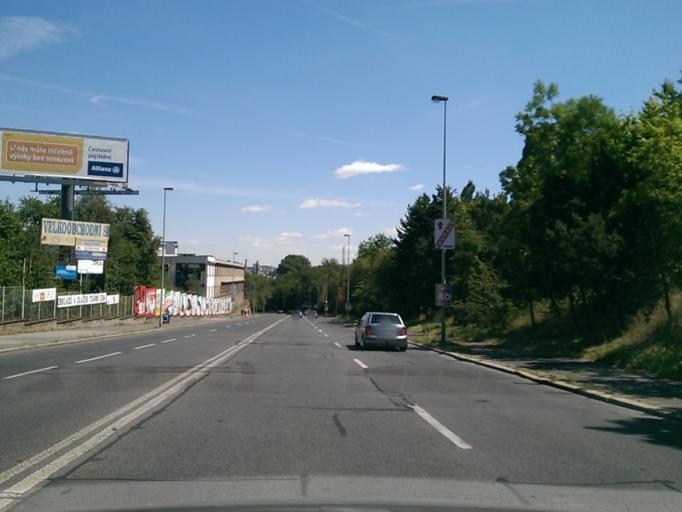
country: CZ
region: Praha
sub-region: Praha 9
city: Prosek
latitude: 50.0996
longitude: 14.4978
